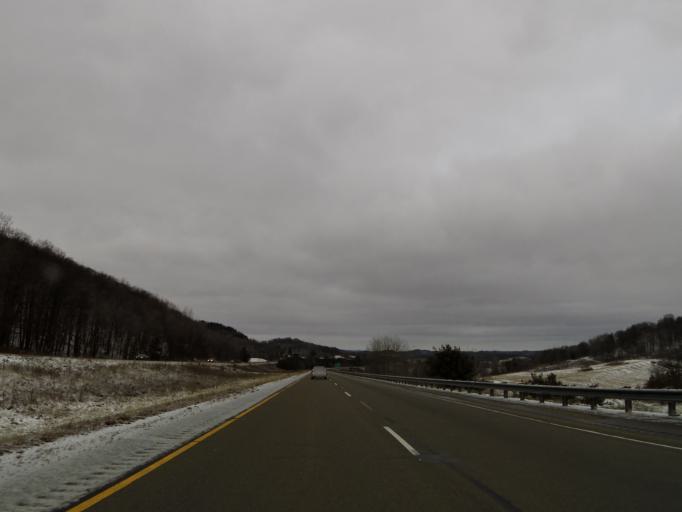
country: US
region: Wisconsin
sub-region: Trempealeau County
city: Osseo
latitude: 44.4385
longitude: -91.0728
